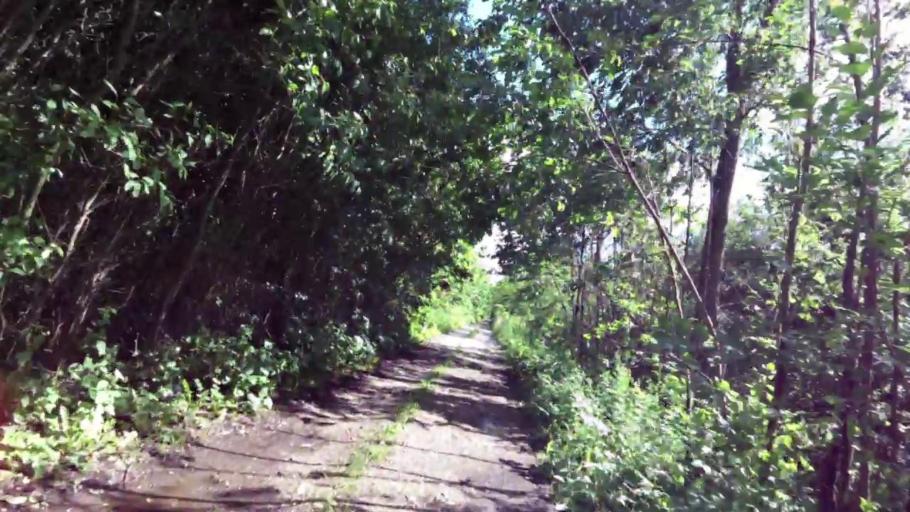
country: PL
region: West Pomeranian Voivodeship
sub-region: Powiat slawienski
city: Slawno
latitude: 54.5024
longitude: 16.7049
